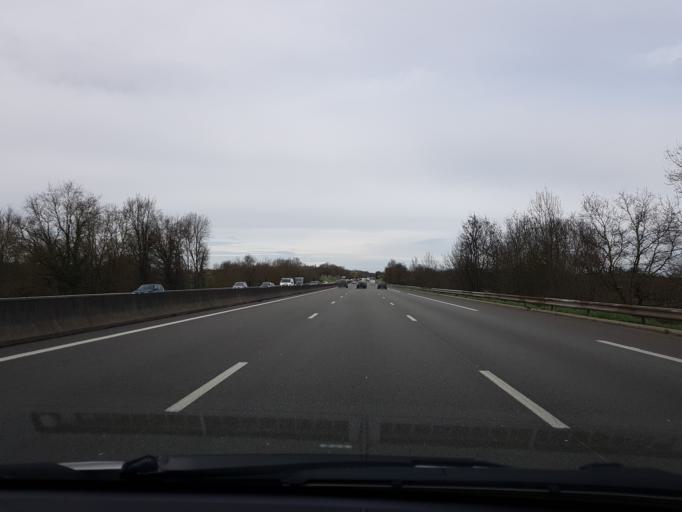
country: FR
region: Bourgogne
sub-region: Departement de Saone-et-Loire
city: Saint-Martin-Belle-Roche
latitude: 46.4354
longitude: 4.8698
